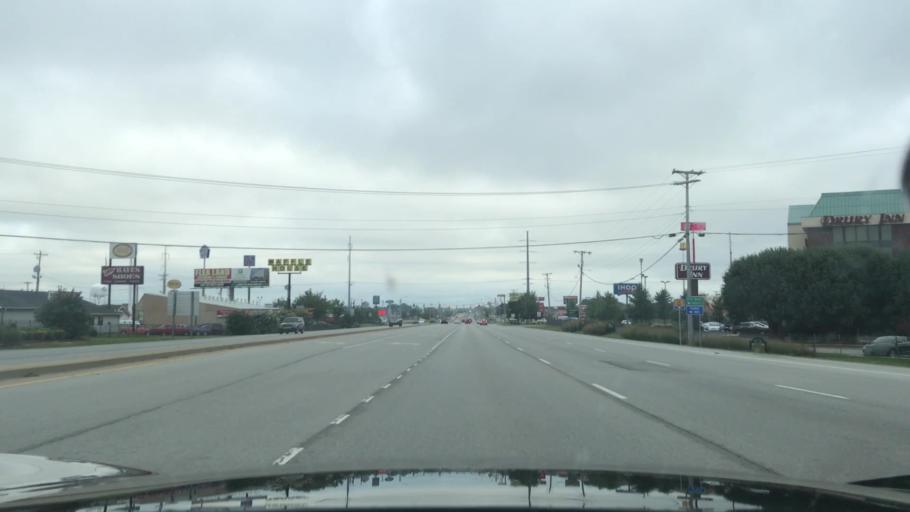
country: US
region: Kentucky
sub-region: Warren County
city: Plano
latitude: 36.9376
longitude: -86.4194
